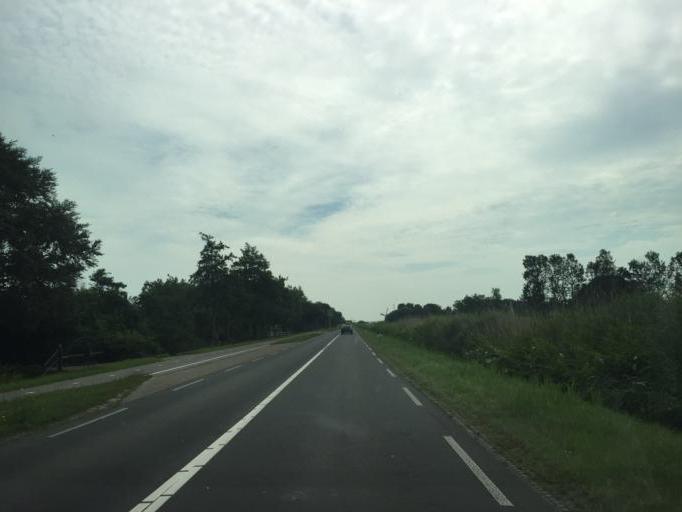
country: NL
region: North Holland
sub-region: Gemeente Heerhugowaard
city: Heerhugowaard
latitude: 52.6033
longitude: 4.8611
